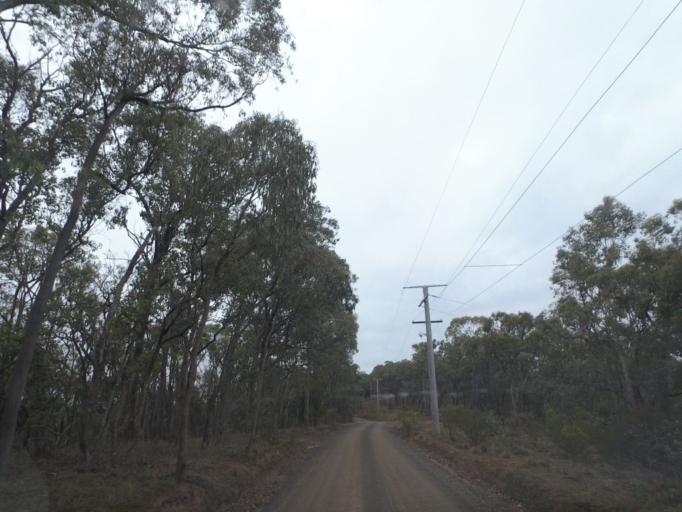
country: AU
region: Victoria
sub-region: Nillumbik
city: Saint Andrews
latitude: -37.6050
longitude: 145.2842
